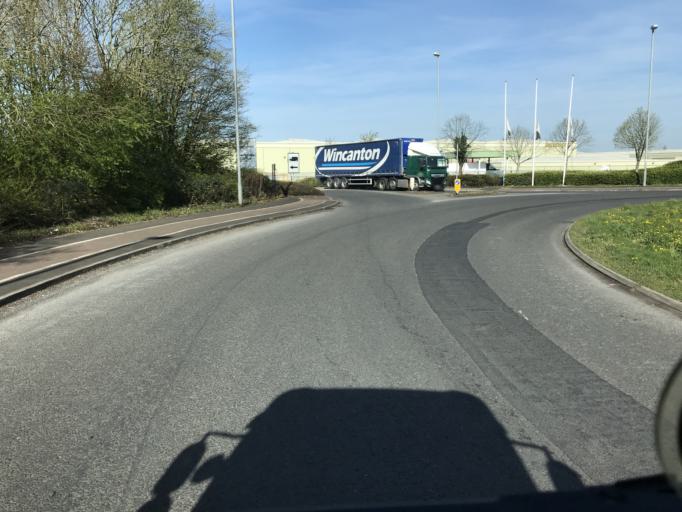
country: GB
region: England
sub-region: Cheshire West and Chester
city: Marston
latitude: 53.2462
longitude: -2.4713
